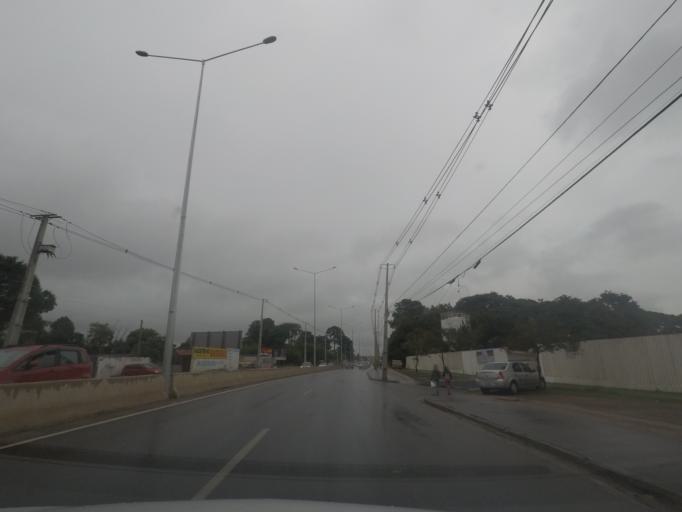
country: BR
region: Parana
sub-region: Piraquara
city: Piraquara
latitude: -25.4534
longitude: -49.0724
